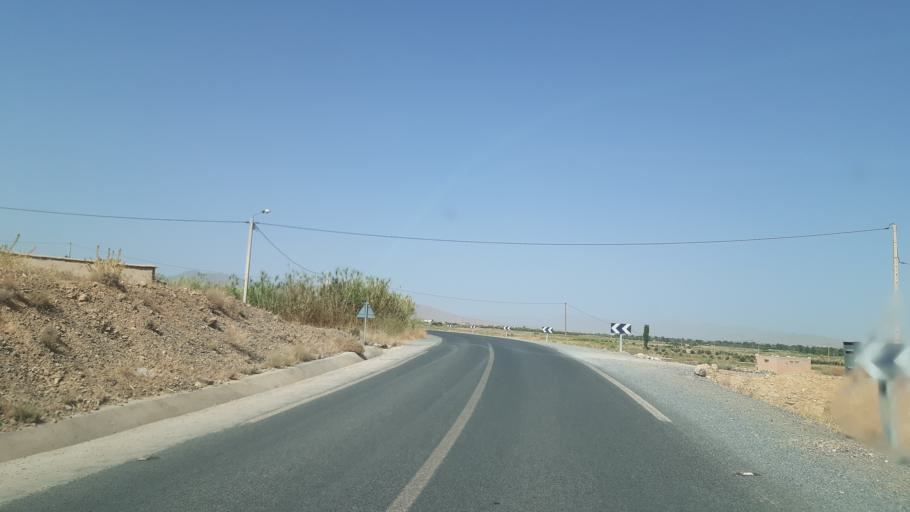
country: MA
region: Meknes-Tafilalet
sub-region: Errachidia
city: Amouguer
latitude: 32.2452
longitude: -4.5909
